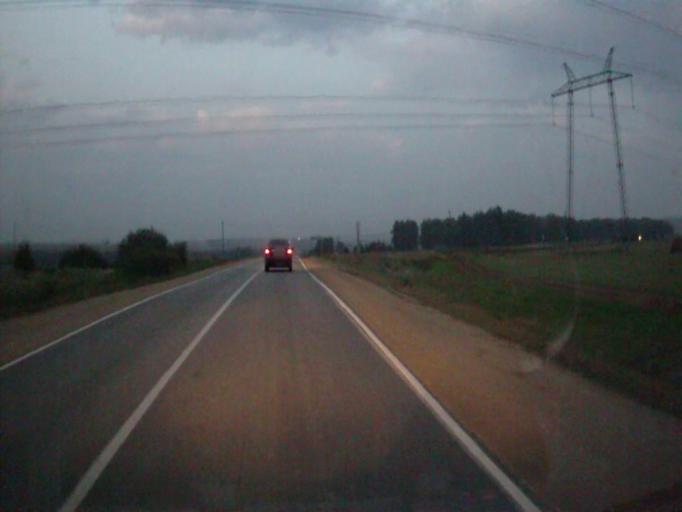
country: RU
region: Chelyabinsk
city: Argayash
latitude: 55.2093
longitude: 60.8781
